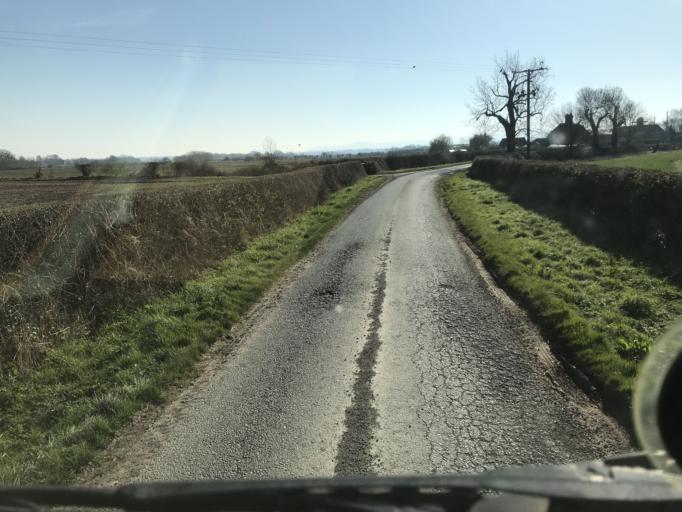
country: GB
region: England
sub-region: Cheshire West and Chester
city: Aldford
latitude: 53.1266
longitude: -2.8542
